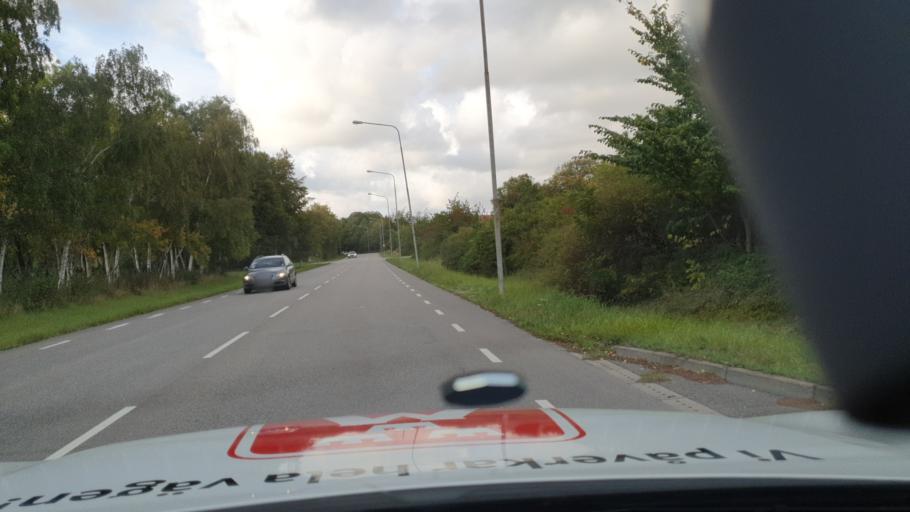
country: SE
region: Skane
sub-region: Vellinge Kommun
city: Vellinge
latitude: 55.4644
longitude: 13.0183
